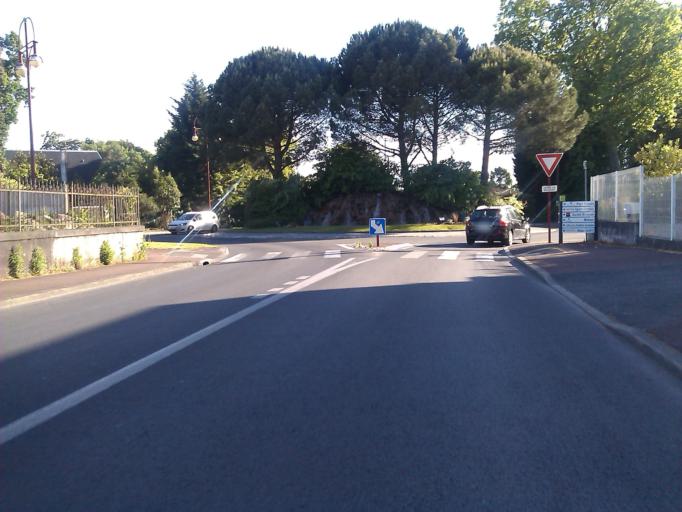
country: FR
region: Aquitaine
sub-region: Departement de la Gironde
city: Pessac
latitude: 44.8034
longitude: -0.6381
